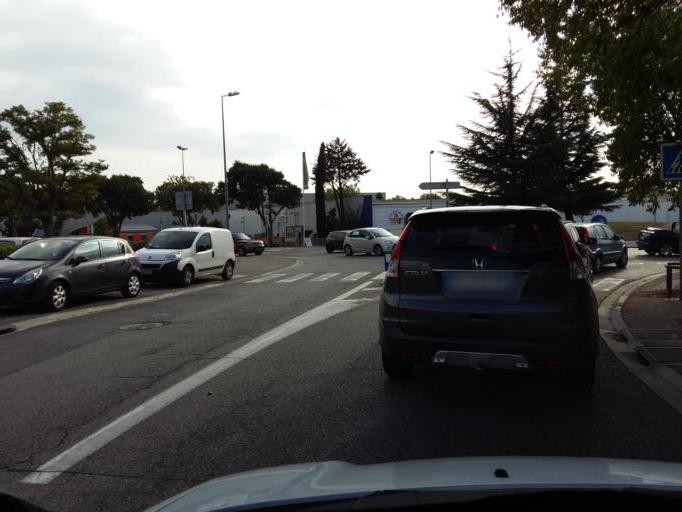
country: FR
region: Provence-Alpes-Cote d'Azur
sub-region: Departement des Bouches-du-Rhone
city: Cabries
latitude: 43.4884
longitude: 5.3778
